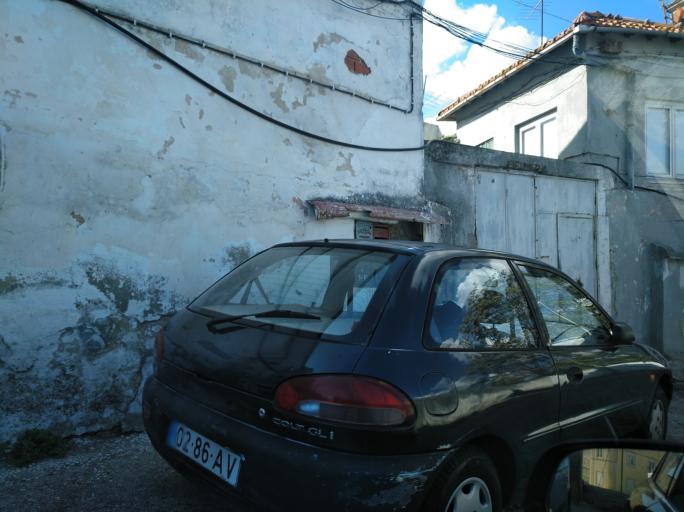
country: PT
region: Lisbon
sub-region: Lisbon
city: Lisbon
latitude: 38.7219
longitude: -9.1255
